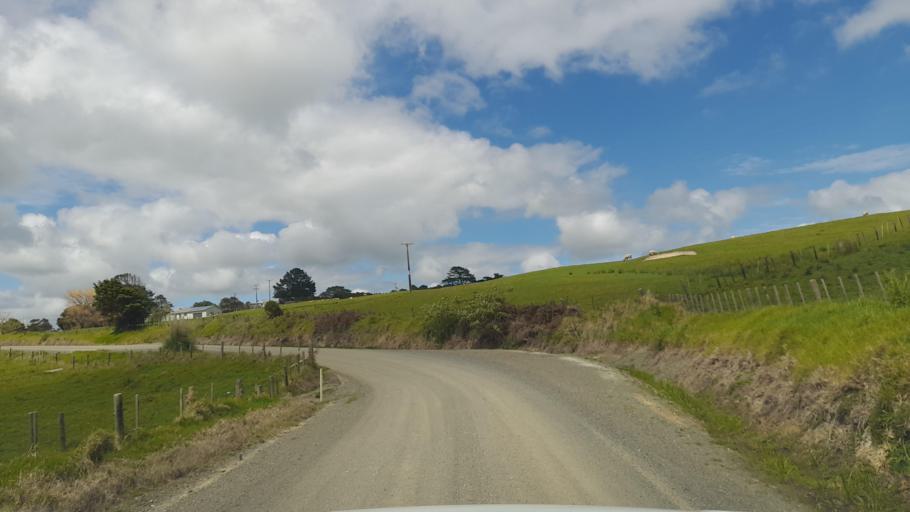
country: NZ
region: Auckland
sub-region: Auckland
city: Wellsford
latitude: -36.1962
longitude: 174.3358
